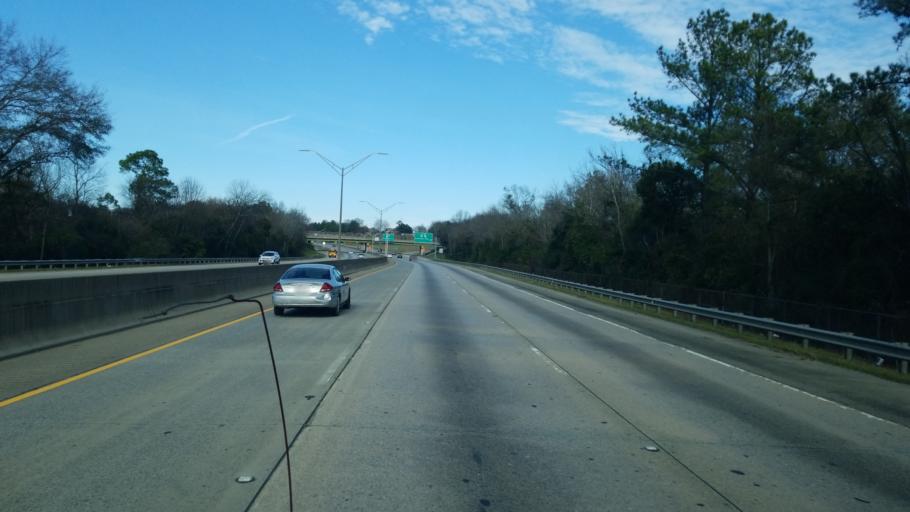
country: US
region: Georgia
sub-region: Bibb County
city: Macon
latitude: 32.8077
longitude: -83.6570
